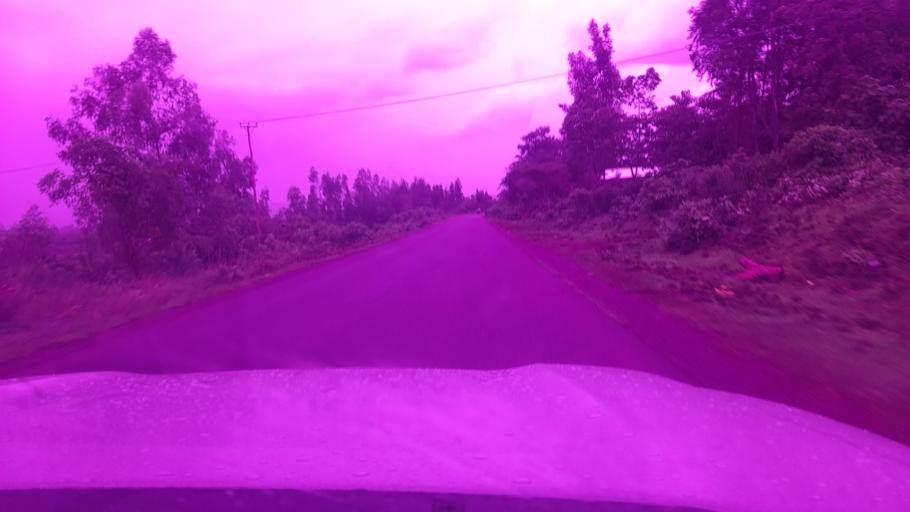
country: ET
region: Oromiya
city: Jima
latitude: 7.7087
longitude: 37.0358
